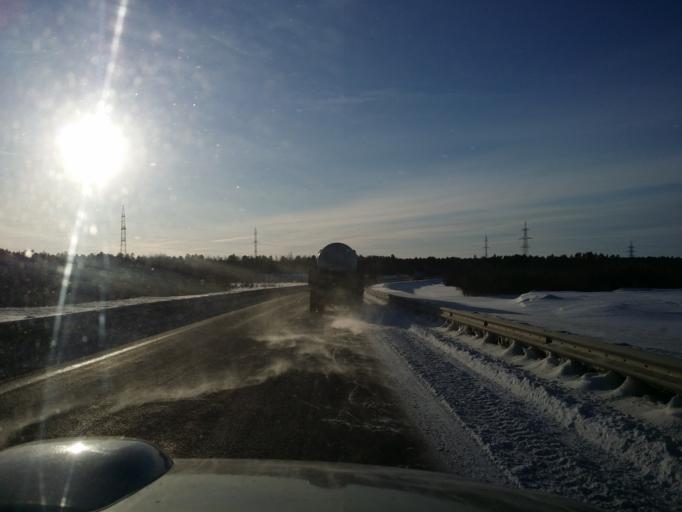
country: RU
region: Khanty-Mansiyskiy Avtonomnyy Okrug
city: Izluchinsk
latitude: 60.9352
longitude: 76.8768
